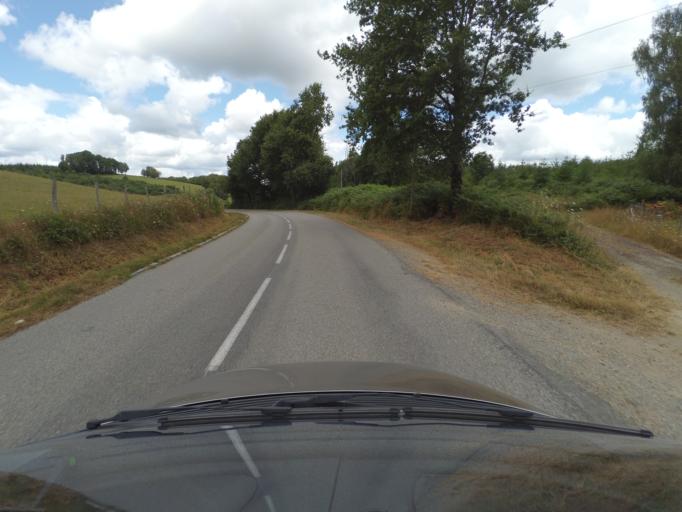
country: FR
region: Limousin
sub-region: Departement de la Creuse
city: Bourganeuf
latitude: 45.9383
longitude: 1.7938
